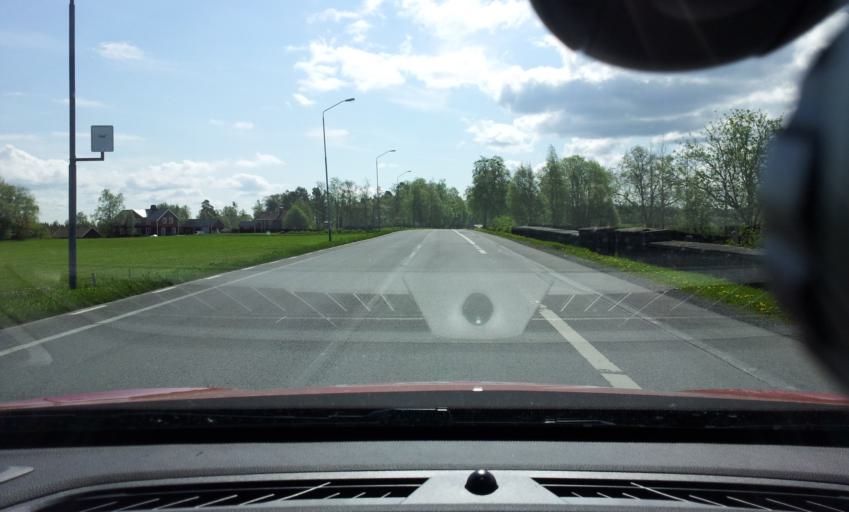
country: SE
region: Jaemtland
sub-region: OEstersunds Kommun
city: Ostersund
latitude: 63.1813
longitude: 14.5145
